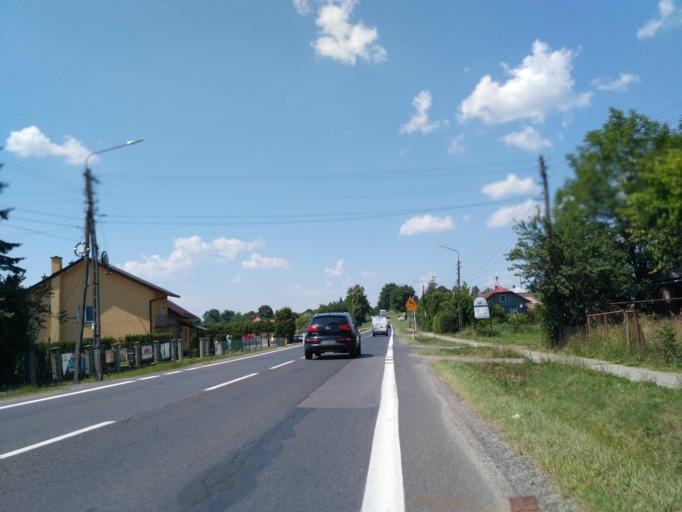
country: PL
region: Subcarpathian Voivodeship
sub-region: Powiat brzozowski
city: Grabownica Starzenska
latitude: 49.6620
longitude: 22.0736
